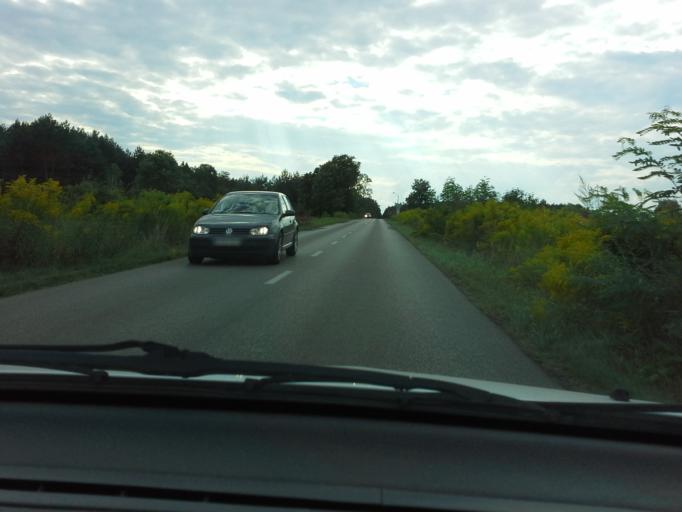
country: PL
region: Lesser Poland Voivodeship
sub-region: Powiat chrzanowski
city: Plaza
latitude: 50.1210
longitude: 19.4559
